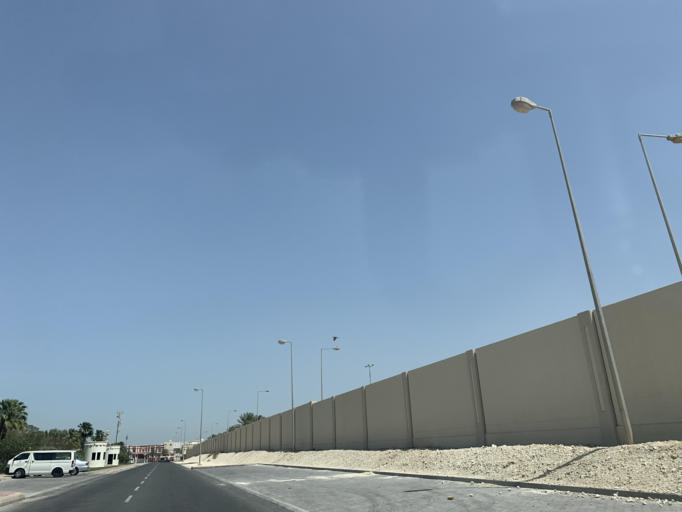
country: BH
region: Northern
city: Ar Rifa'
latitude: 26.1427
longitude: 50.5512
